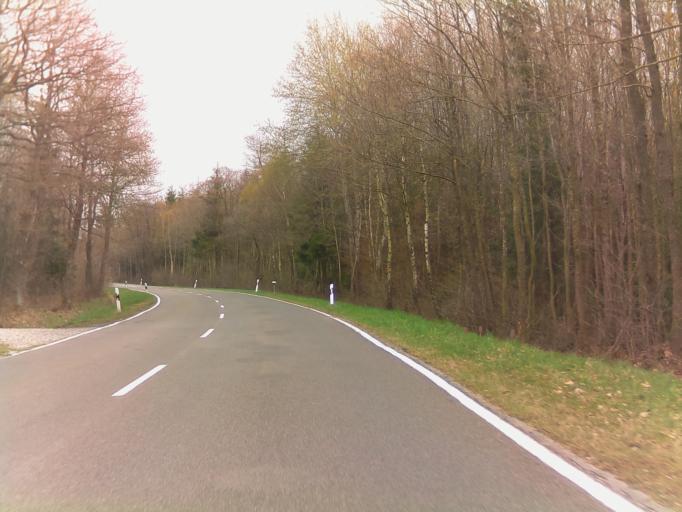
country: DE
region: Rheinland-Pfalz
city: Weitersborn
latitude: 49.8746
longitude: 7.5336
